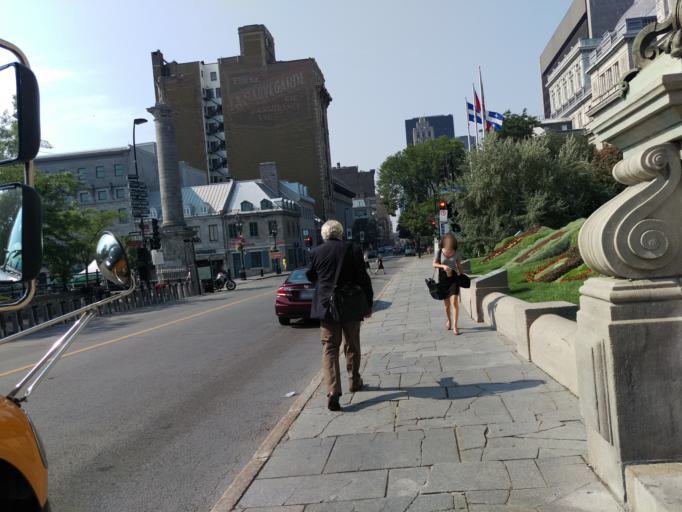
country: CA
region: Quebec
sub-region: Montreal
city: Montreal
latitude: 45.5087
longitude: -73.5538
